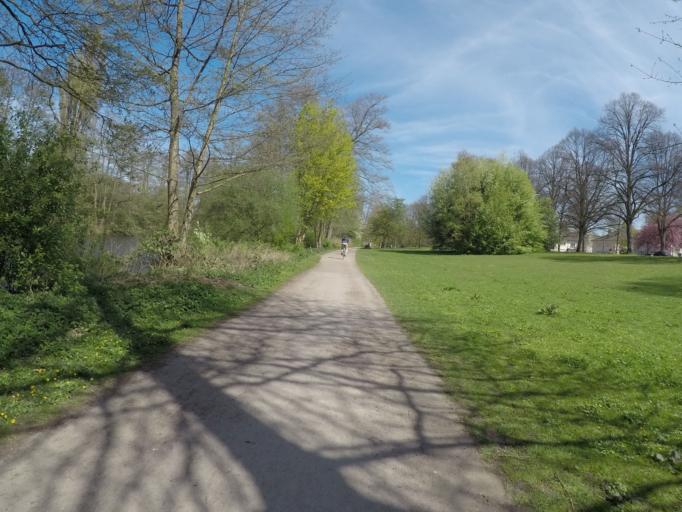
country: DE
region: Hamburg
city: Alsterdorf
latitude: 53.6175
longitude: 10.0227
